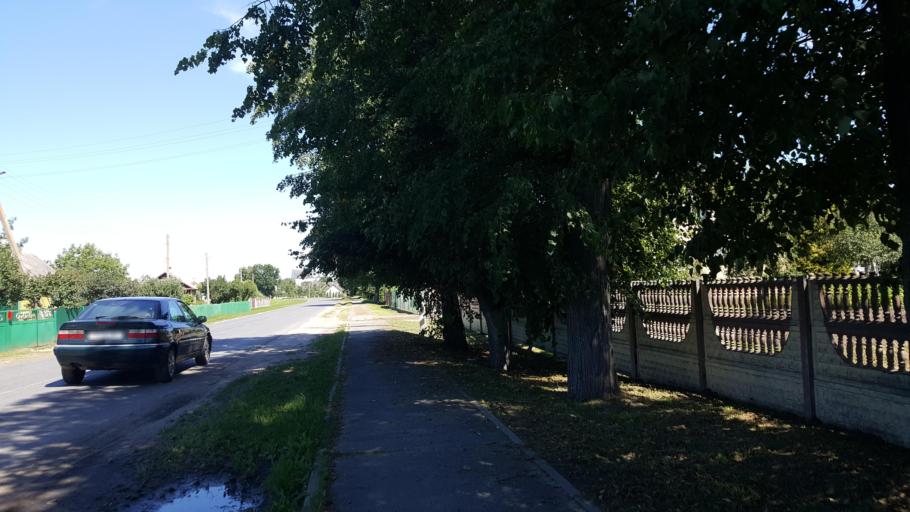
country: BY
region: Brest
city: Charnawchytsy
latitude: 52.2118
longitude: 23.7383
